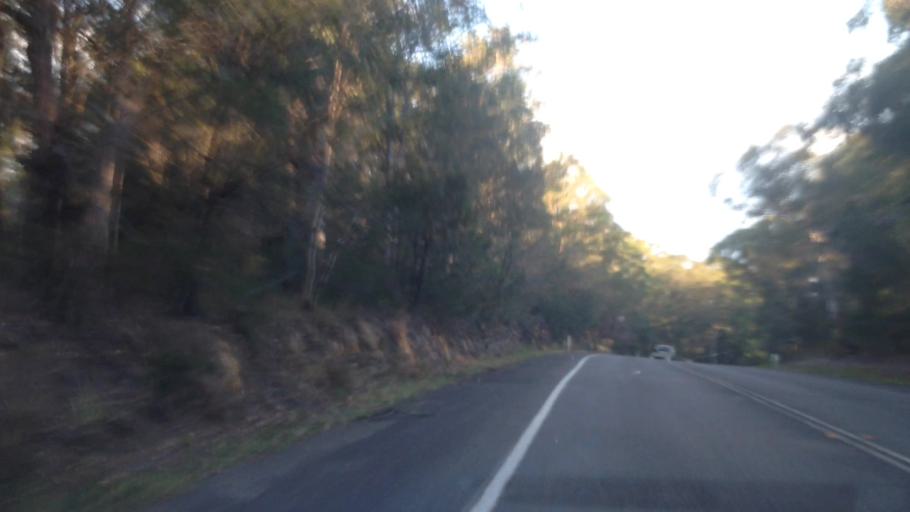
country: AU
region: New South Wales
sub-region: Lake Macquarie Shire
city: Cooranbong
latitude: -33.0567
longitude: 151.4747
